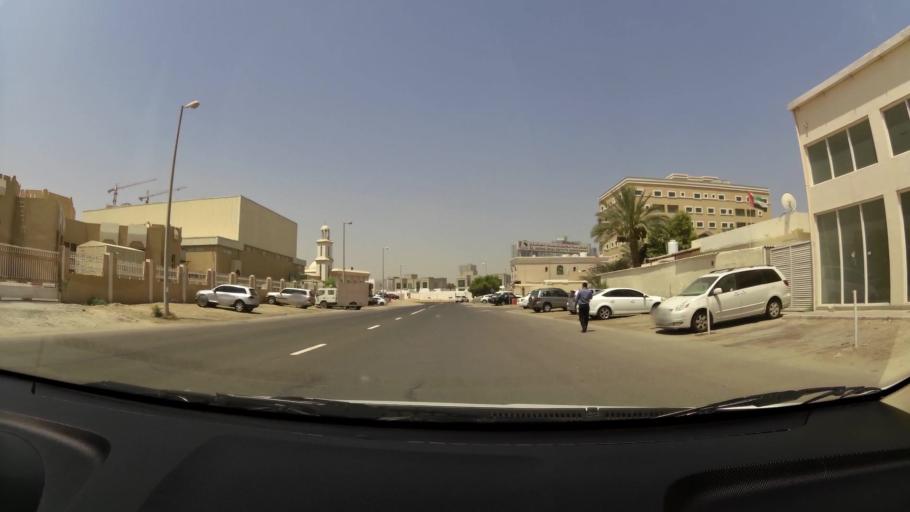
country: AE
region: Ajman
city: Ajman
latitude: 25.3933
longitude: 55.4496
